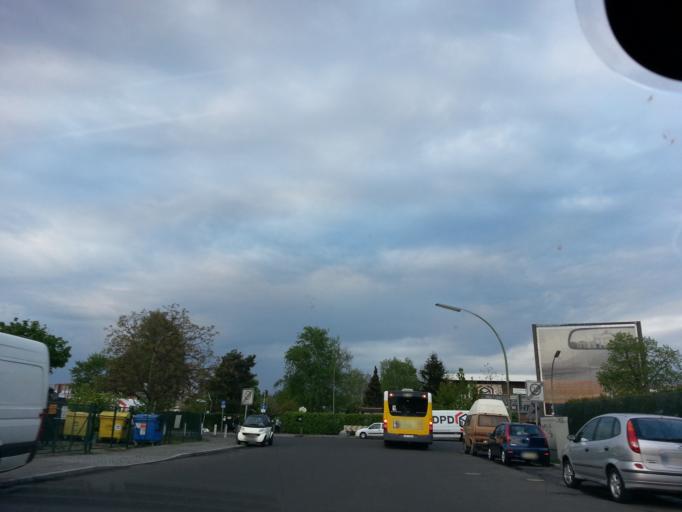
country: DE
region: Berlin
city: Charlottenburg-Nord
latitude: 52.5409
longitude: 13.3147
